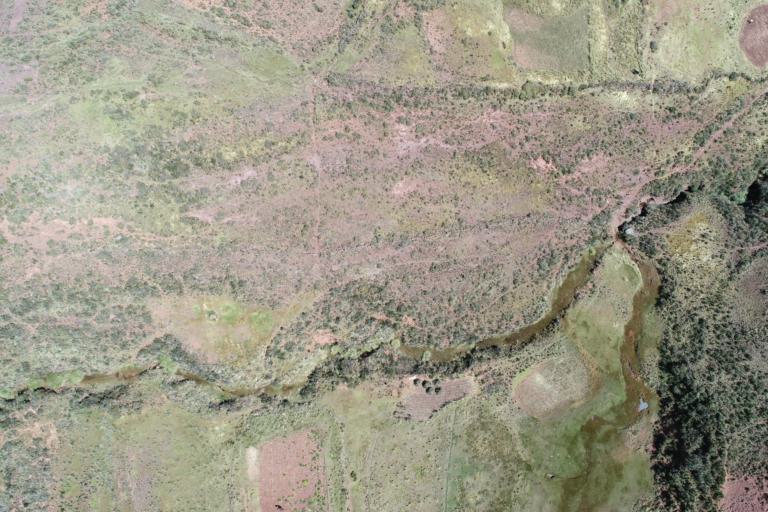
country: BO
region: La Paz
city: Tiahuanaco
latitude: -16.6068
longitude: -68.7608
